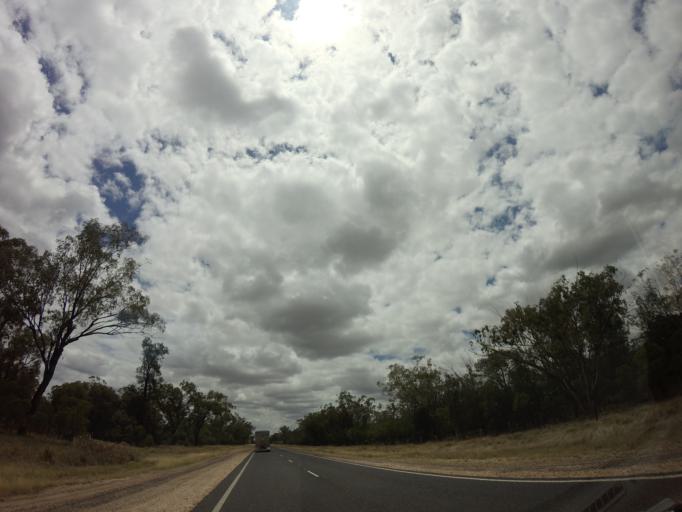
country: AU
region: Queensland
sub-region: Goondiwindi
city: Goondiwindi
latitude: -28.4378
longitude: 150.3009
